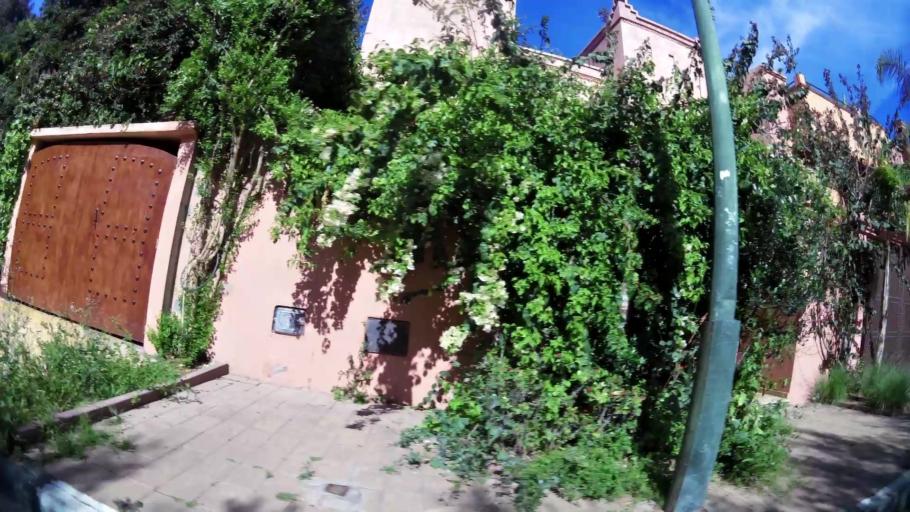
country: MA
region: Marrakech-Tensift-Al Haouz
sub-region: Marrakech
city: Marrakesh
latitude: 31.6544
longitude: -8.0536
